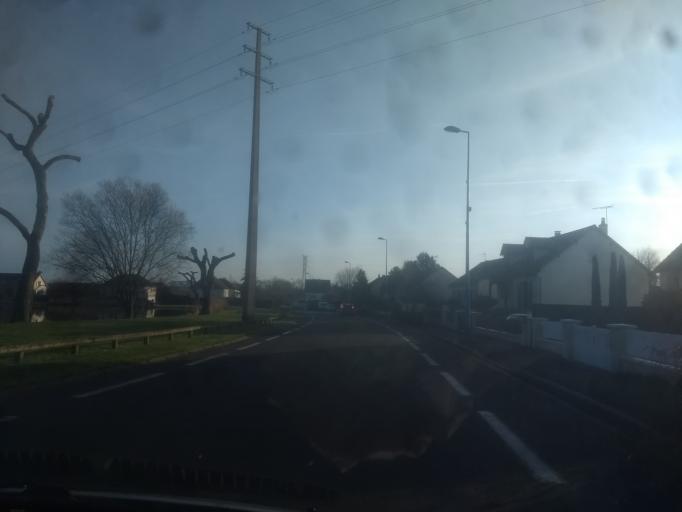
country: FR
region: Centre
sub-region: Departement du Cher
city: Bourges
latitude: 47.1105
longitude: 2.3833
